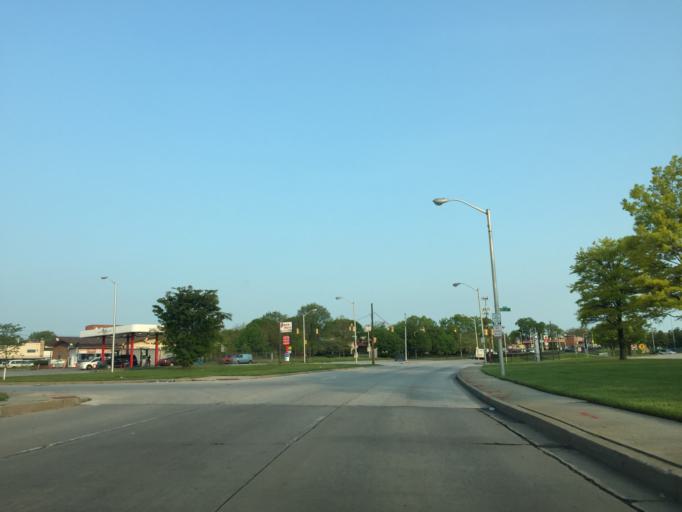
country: US
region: Maryland
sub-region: Baltimore County
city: Lochearn
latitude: 39.3348
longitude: -76.6710
